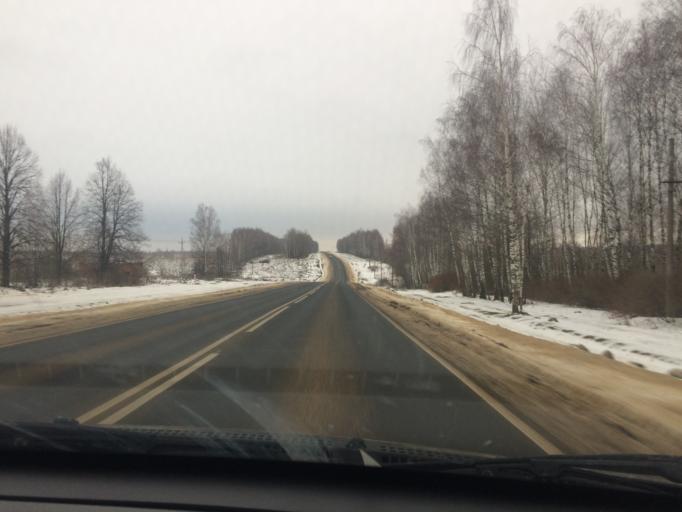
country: RU
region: Tula
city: Shvartsevskiy
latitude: 54.3214
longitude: 37.9721
